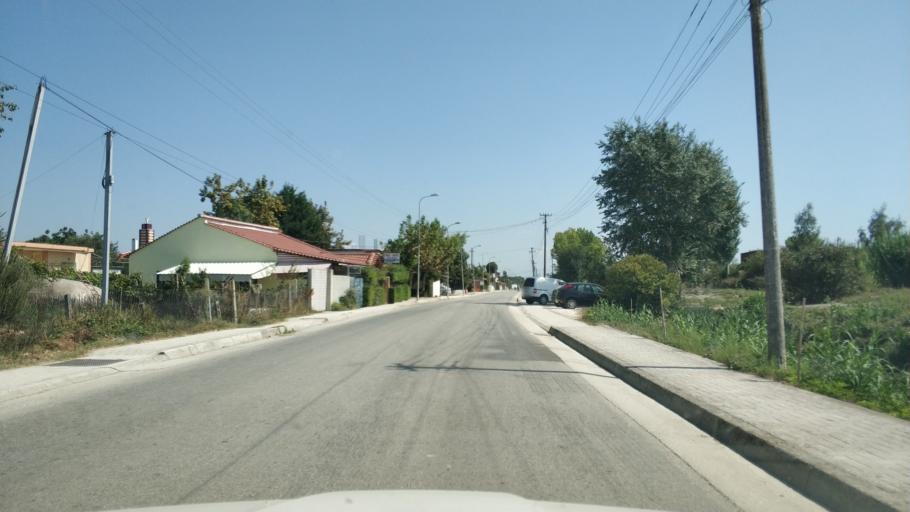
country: AL
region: Fier
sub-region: Rrethi i Lushnjes
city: Gradishte
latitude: 40.8934
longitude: 19.6206
